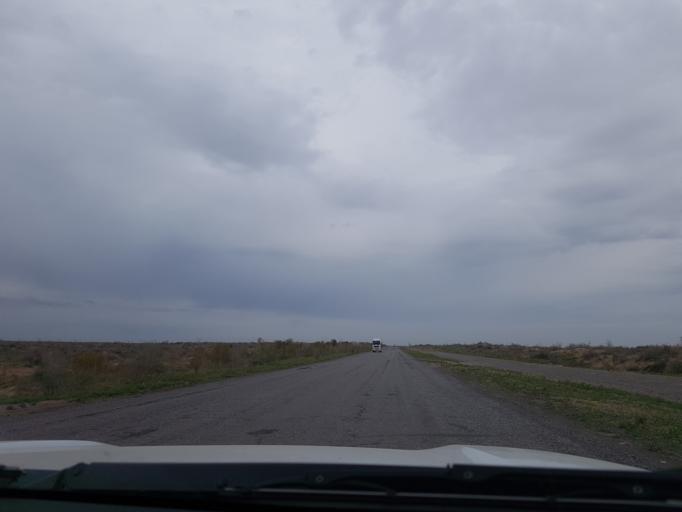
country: TM
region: Lebap
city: Turkmenabat
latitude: 38.9509
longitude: 63.4943
